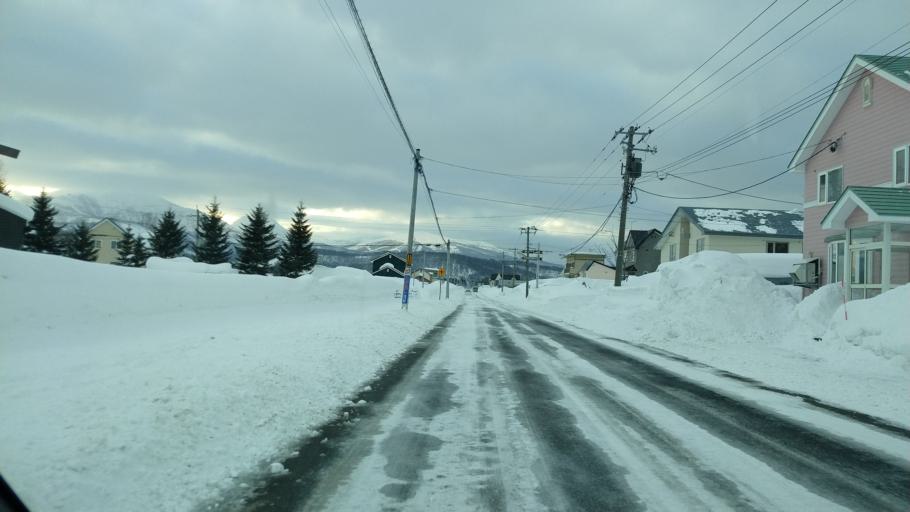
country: JP
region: Hokkaido
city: Niseko Town
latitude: 42.9083
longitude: 140.7679
